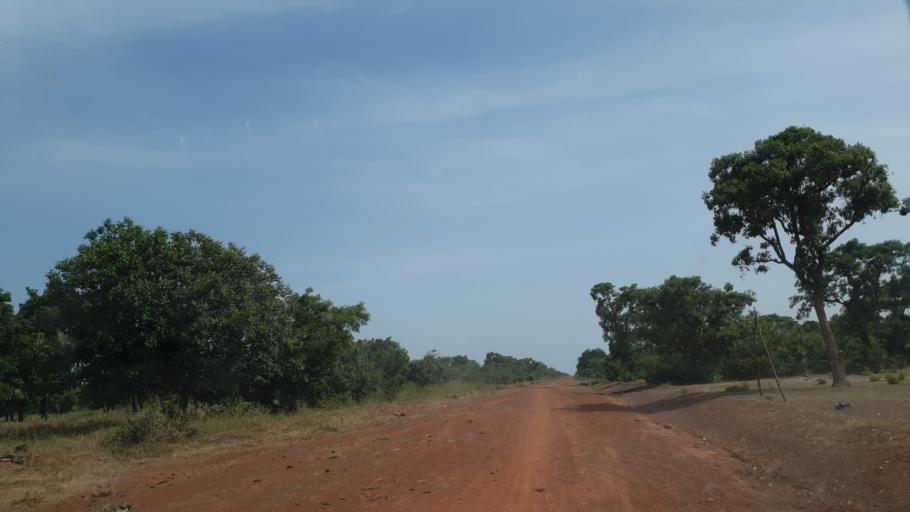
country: ML
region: Koulikoro
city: Dioila
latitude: 12.4333
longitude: -6.2150
